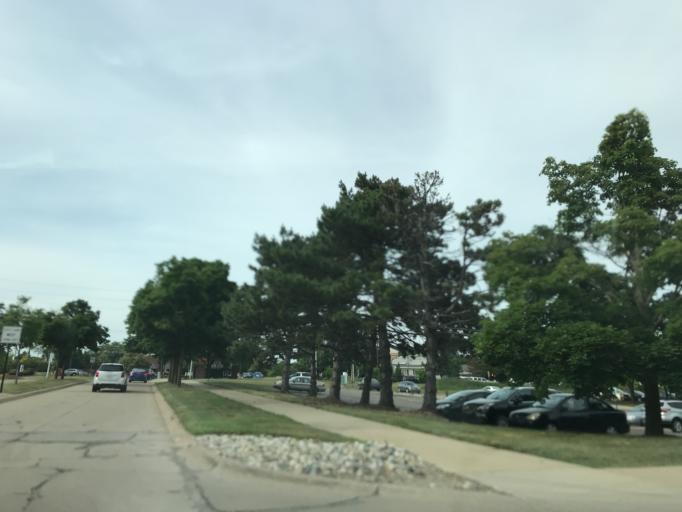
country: US
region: Michigan
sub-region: Wayne County
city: Plymouth
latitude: 42.4095
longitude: -83.4287
